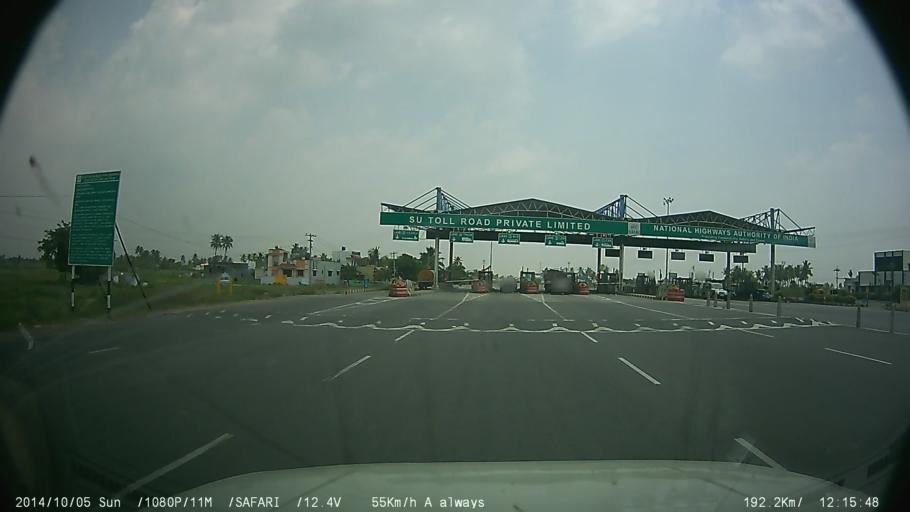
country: IN
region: Tamil Nadu
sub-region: Villupuram
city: Kallakkurichchi
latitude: 11.7366
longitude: 79.0088
